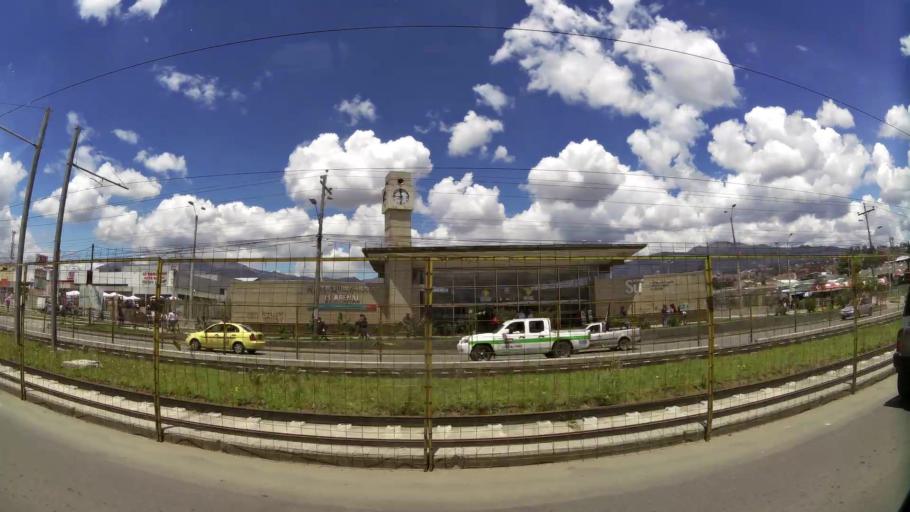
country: EC
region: Azuay
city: Cuenca
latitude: -2.8992
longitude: -79.0267
